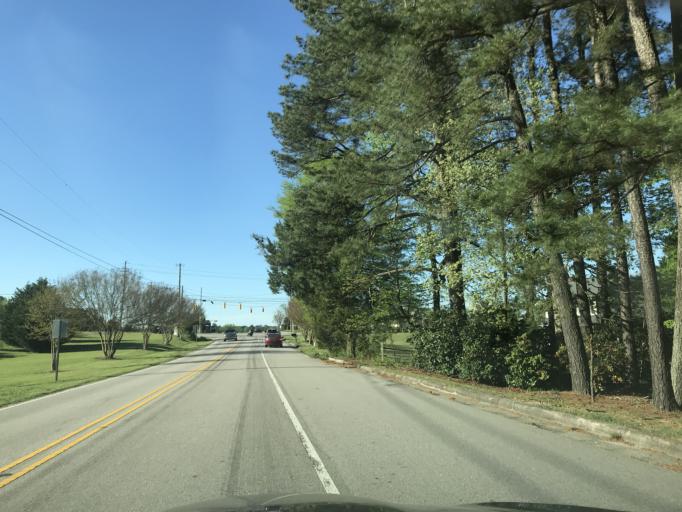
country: US
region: North Carolina
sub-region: Wake County
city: Knightdale
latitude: 35.8329
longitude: -78.5555
